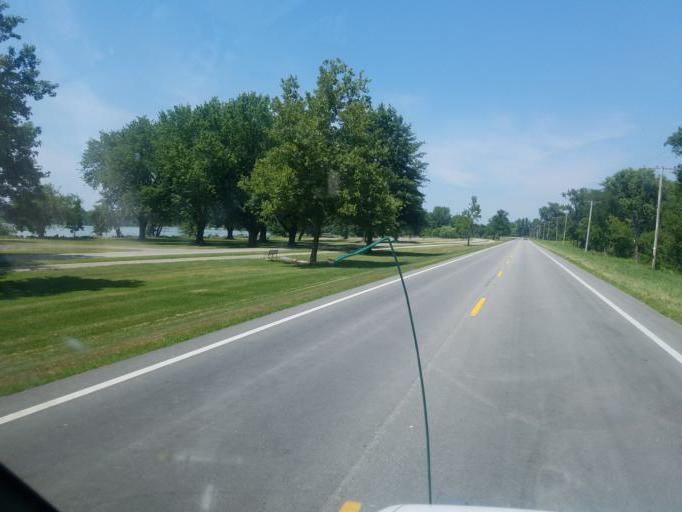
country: US
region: Ohio
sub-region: Auglaize County
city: Saint Marys
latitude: 40.5336
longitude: -84.4176
